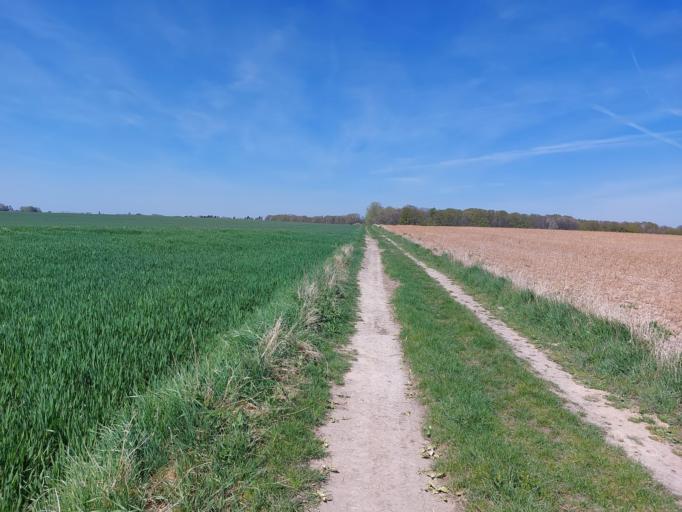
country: BE
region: Wallonia
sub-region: Province du Hainaut
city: Silly
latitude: 50.6104
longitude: 3.9713
